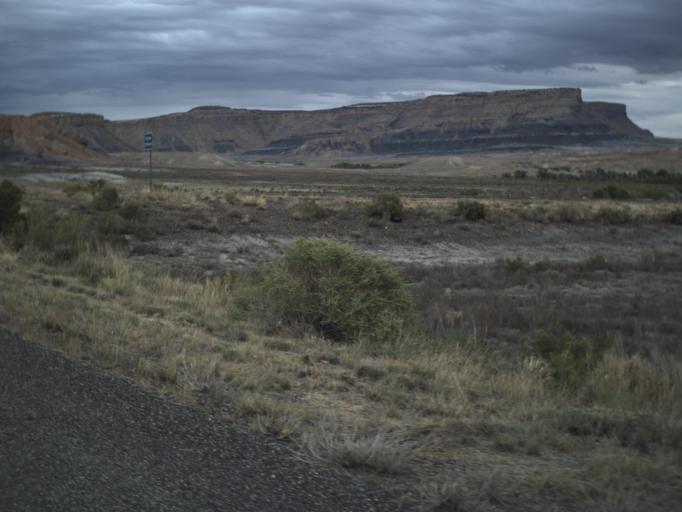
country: US
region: Utah
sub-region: Emery County
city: Ferron
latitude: 38.8094
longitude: -111.2103
